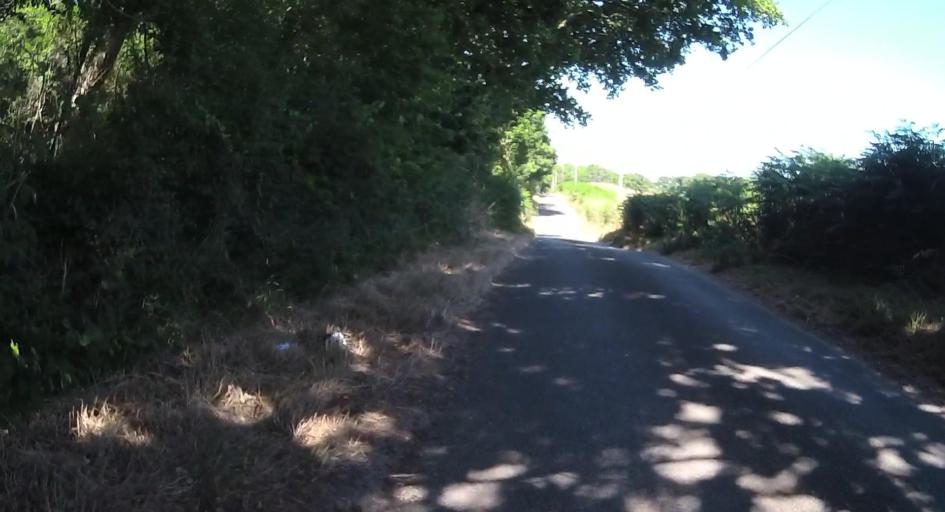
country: GB
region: England
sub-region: Dorset
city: Bovington Camp
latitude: 50.7396
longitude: -2.2246
